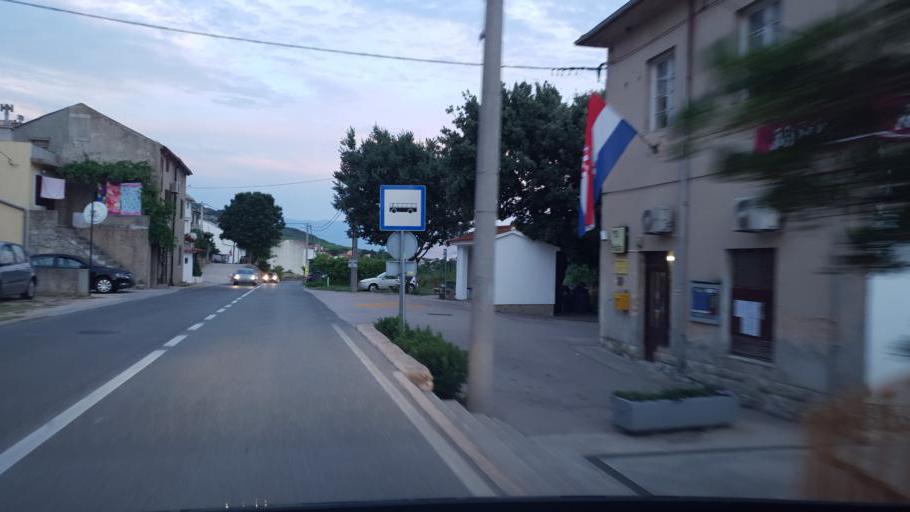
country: HR
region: Primorsko-Goranska
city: Punat
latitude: 44.9949
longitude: 14.7160
